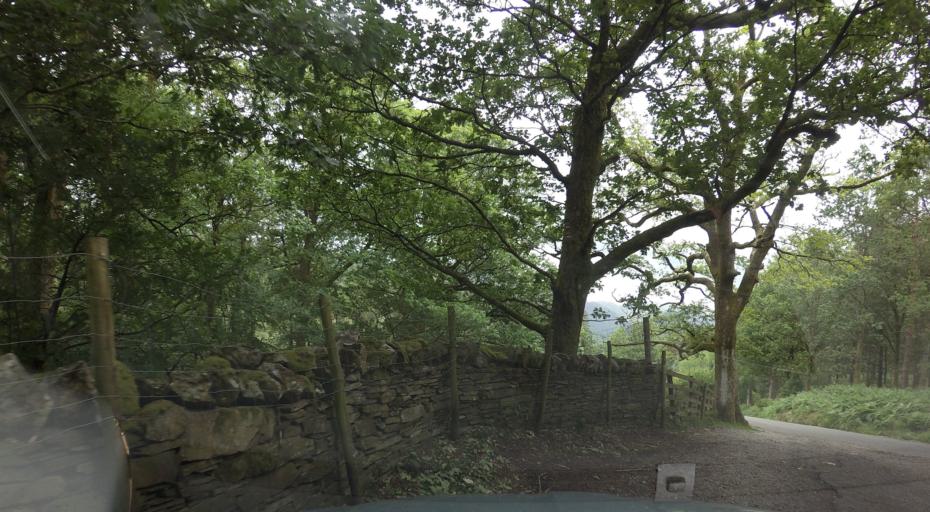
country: GB
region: England
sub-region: Cumbria
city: Keswick
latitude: 54.5595
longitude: -3.1596
